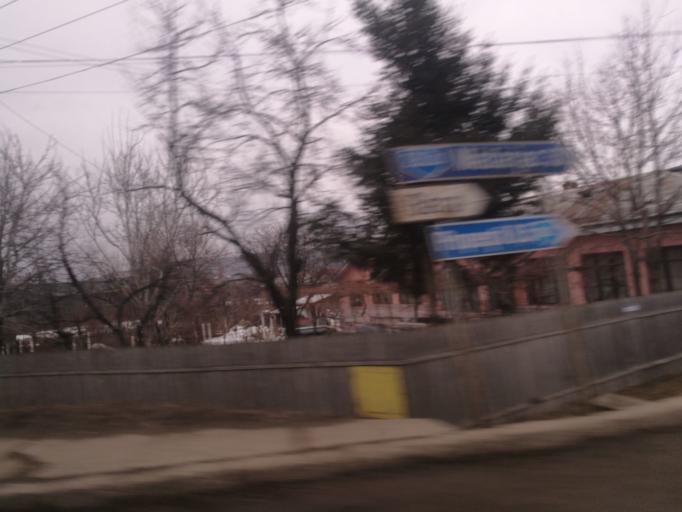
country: RO
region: Iasi
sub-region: Comuna Podu Iloaiei
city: Podu Iloaiei
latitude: 47.2132
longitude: 27.2803
